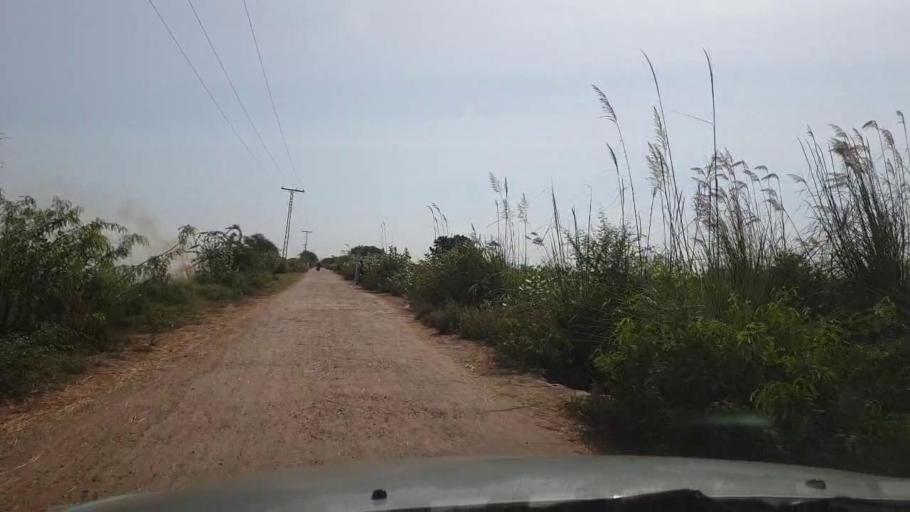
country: PK
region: Sindh
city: Tando Muhammad Khan
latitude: 25.1489
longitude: 68.3926
